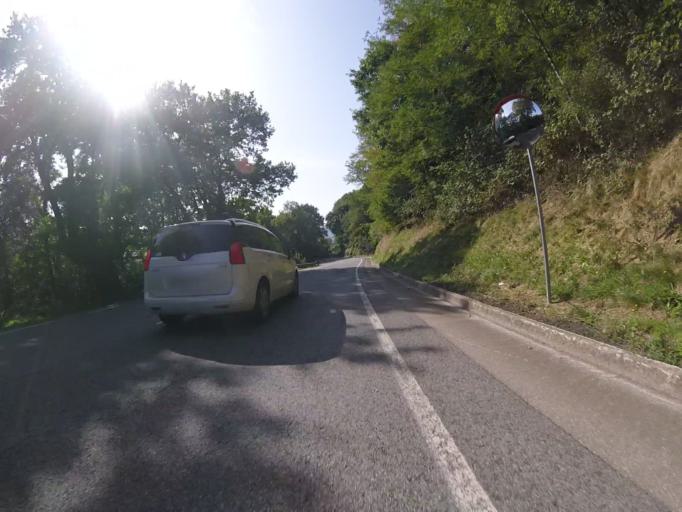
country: ES
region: Navarre
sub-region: Provincia de Navarra
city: Zugarramurdi
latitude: 43.2144
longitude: -1.4905
